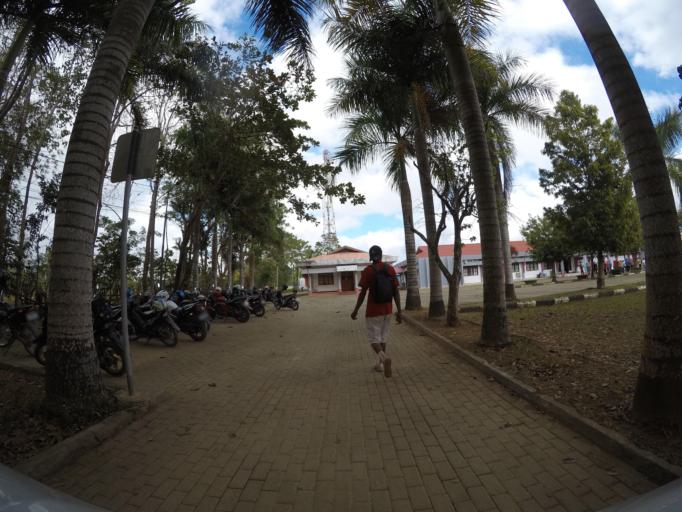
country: TL
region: Lautem
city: Lospalos
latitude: -8.4950
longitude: 126.9915
